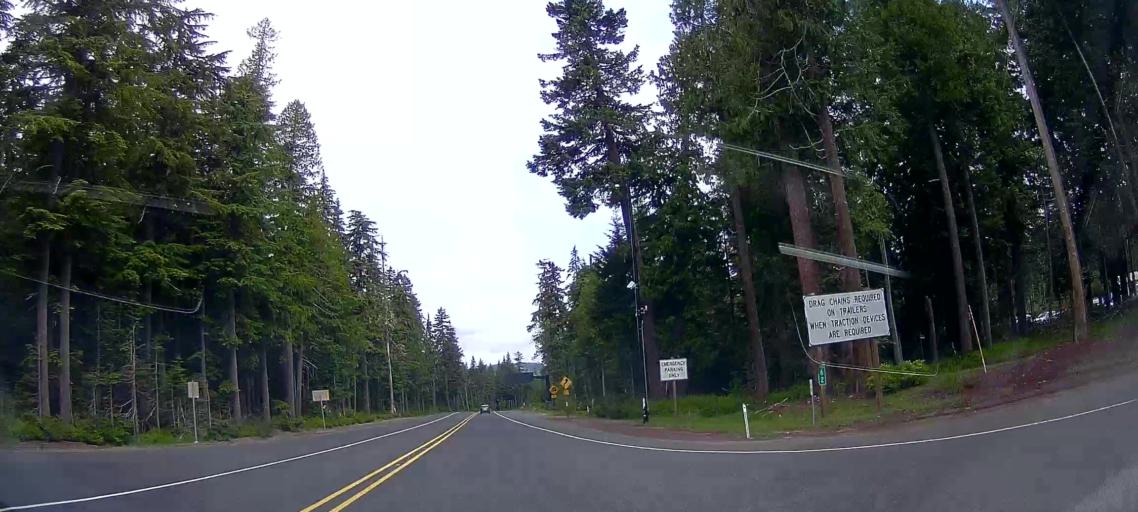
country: US
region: Oregon
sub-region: Clackamas County
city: Mount Hood Village
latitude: 45.2286
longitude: -121.7002
